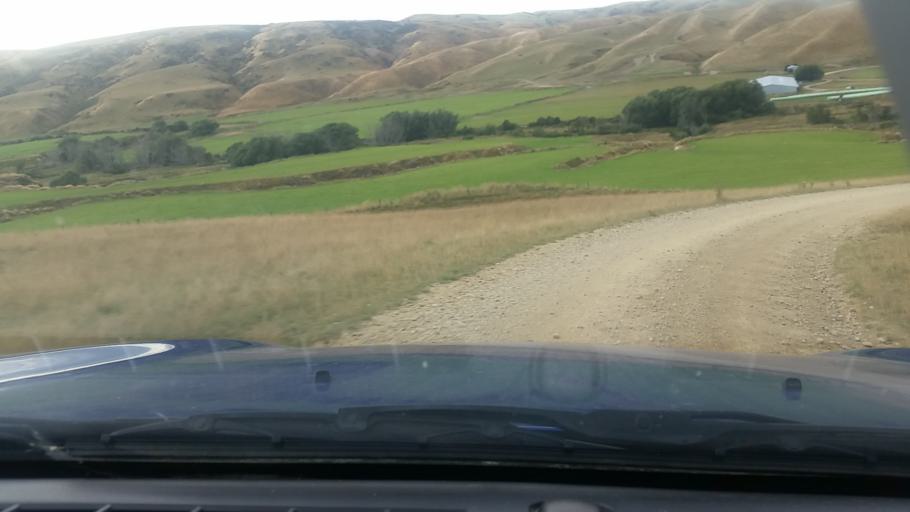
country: NZ
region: Otago
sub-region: Clutha District
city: Balclutha
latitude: -45.7187
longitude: 169.5369
